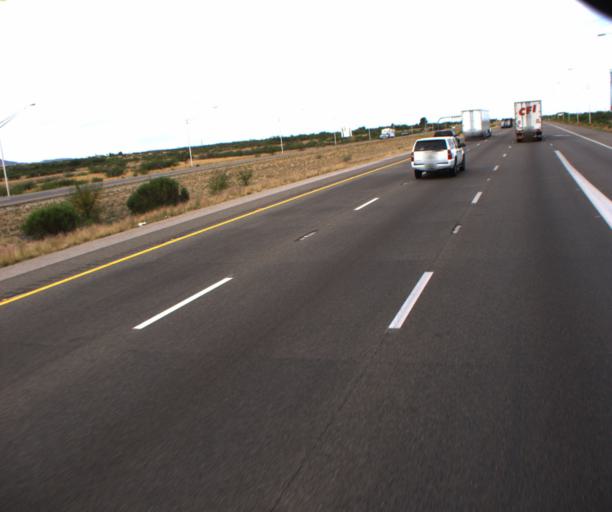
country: US
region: Arizona
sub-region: Cochise County
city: Whetstone
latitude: 31.9636
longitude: -110.3546
